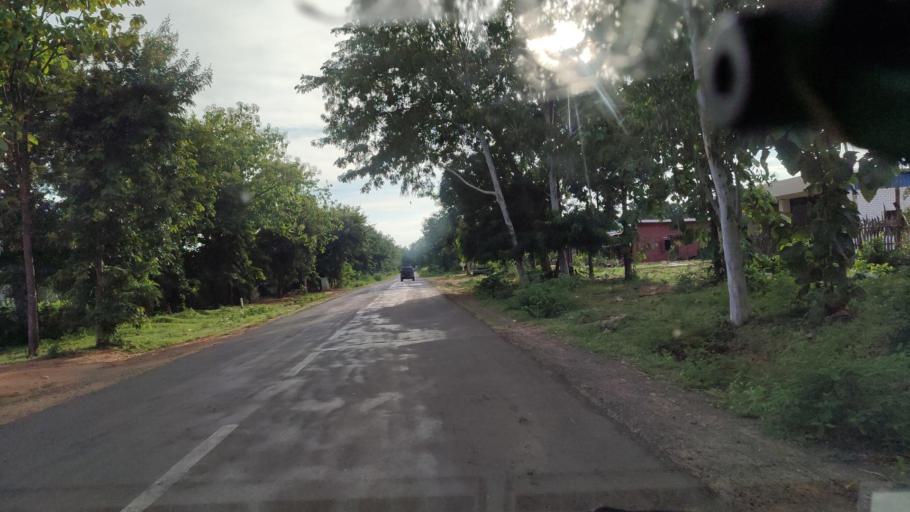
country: MM
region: Magway
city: Chauk
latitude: 20.8130
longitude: 95.0478
